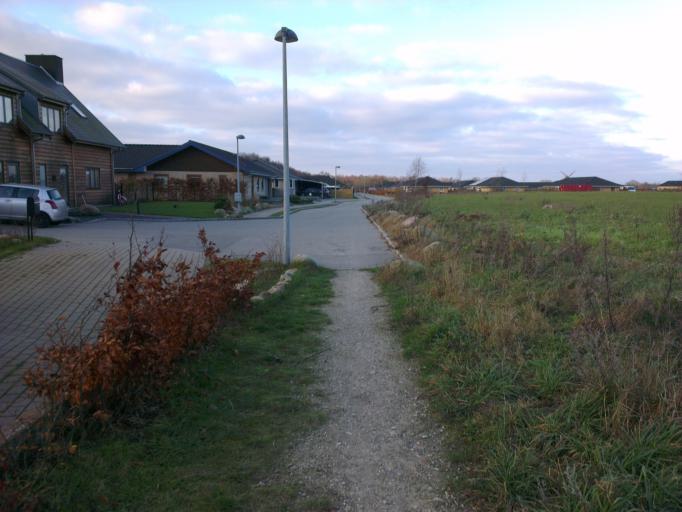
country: DK
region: Capital Region
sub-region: Frederikssund Kommune
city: Jaegerspris
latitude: 55.8461
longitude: 11.9980
